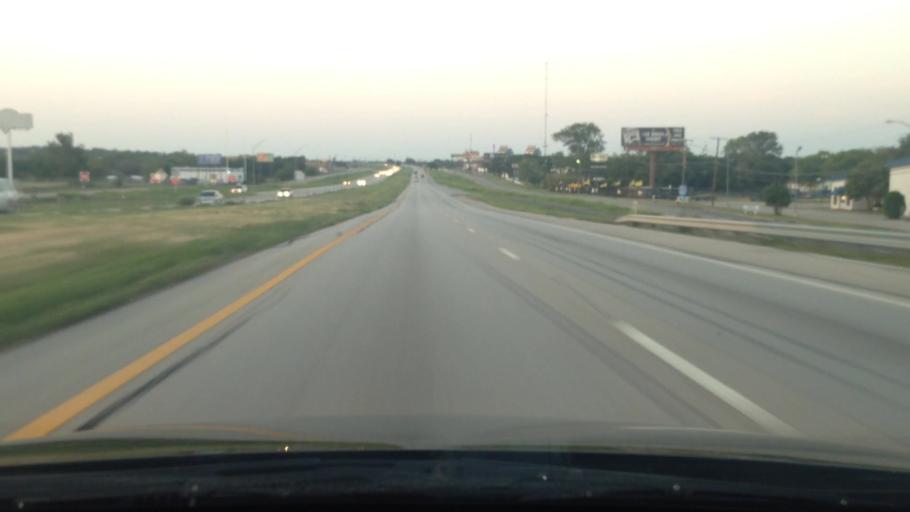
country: US
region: Texas
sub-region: Tarrant County
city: Forest Hill
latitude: 32.7089
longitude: -97.2309
